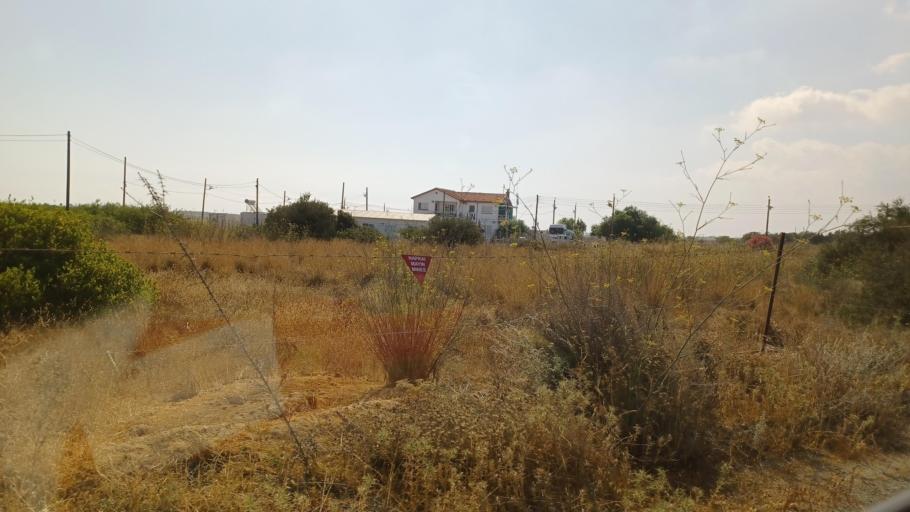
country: CY
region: Ammochostos
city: Deryneia
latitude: 35.0724
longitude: 33.9637
